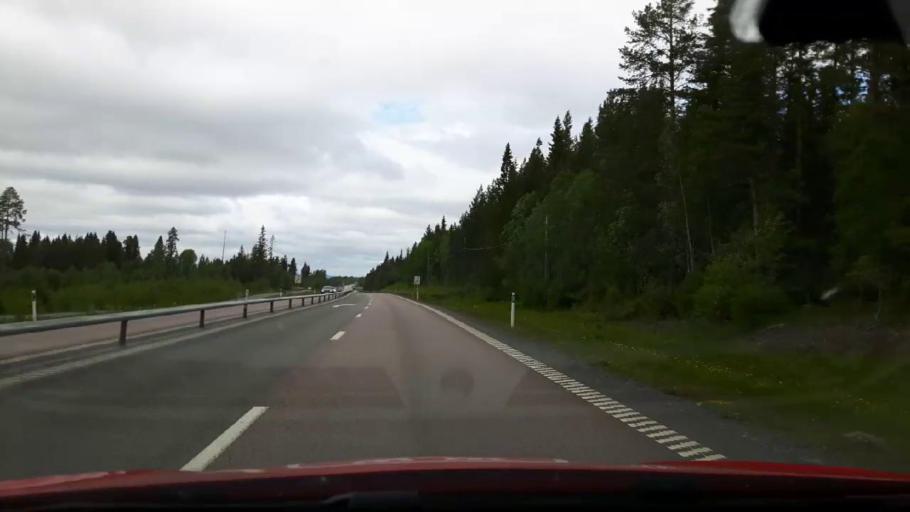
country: SE
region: Jaemtland
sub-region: Krokoms Kommun
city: Krokom
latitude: 63.2763
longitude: 14.5302
